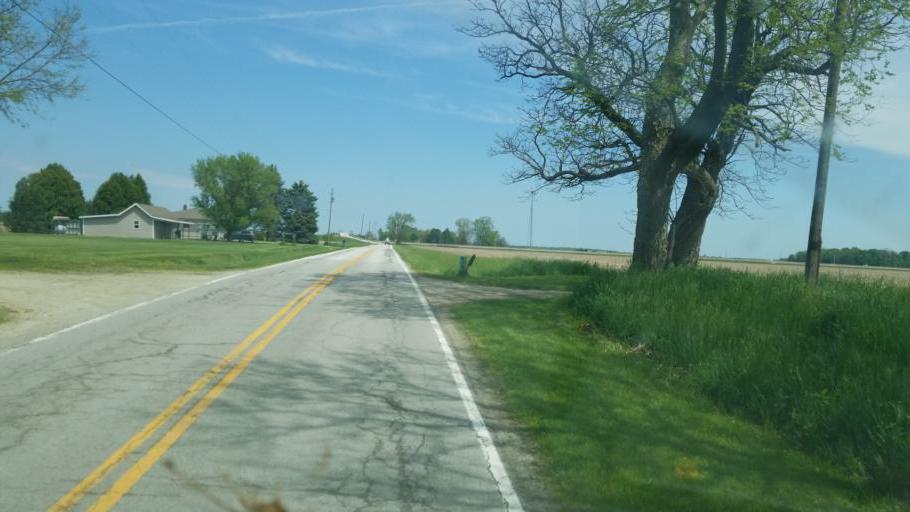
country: US
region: Ohio
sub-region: Sandusky County
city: Stony Prairie
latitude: 41.4246
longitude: -83.2016
